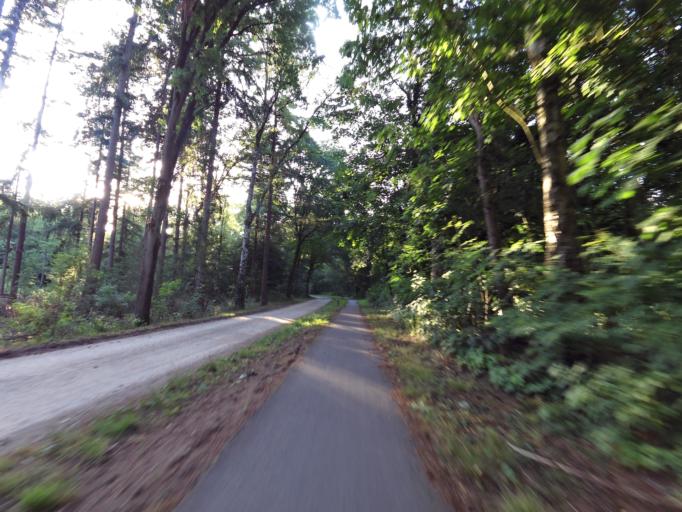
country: NL
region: Gelderland
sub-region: Gemeente Doetinchem
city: Doetinchem
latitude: 51.9936
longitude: 6.2741
